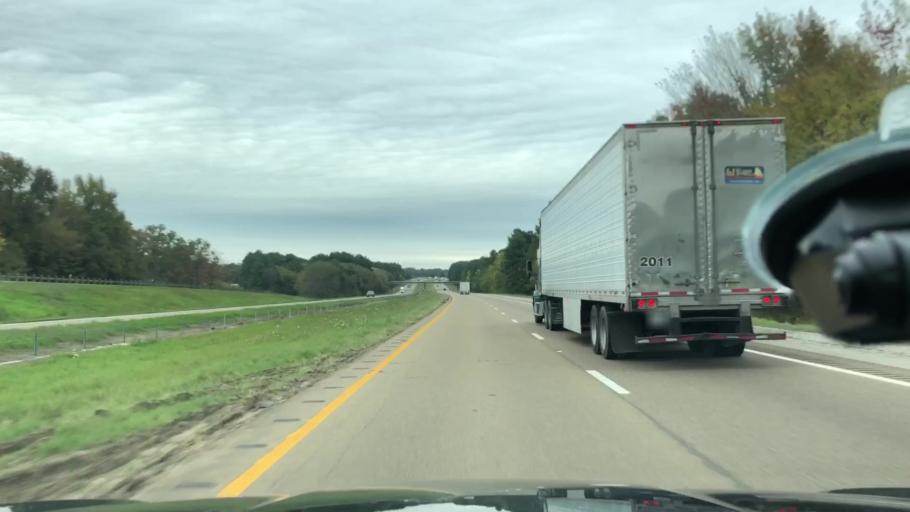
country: US
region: Texas
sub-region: Titus County
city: Mount Pleasant
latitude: 33.2182
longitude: -94.8951
